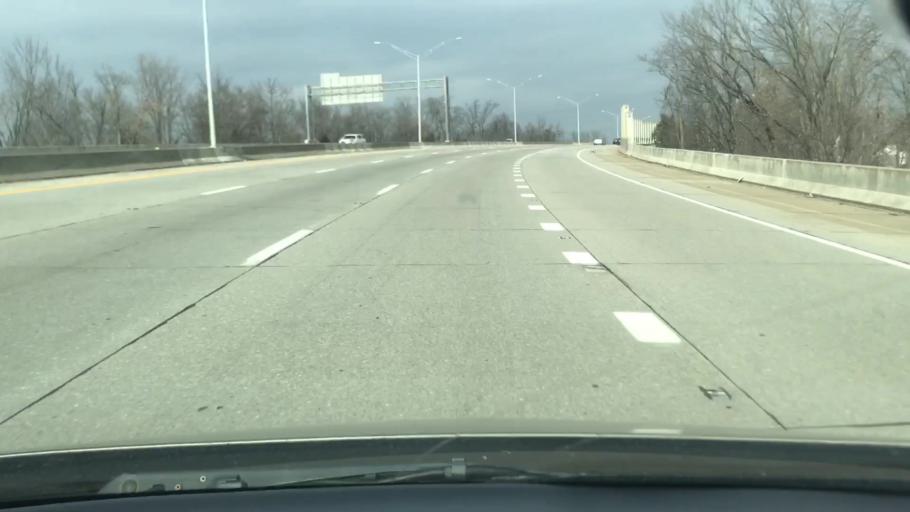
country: US
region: Kentucky
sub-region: Jefferson County
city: Beechwood Village
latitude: 38.2581
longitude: -85.6226
